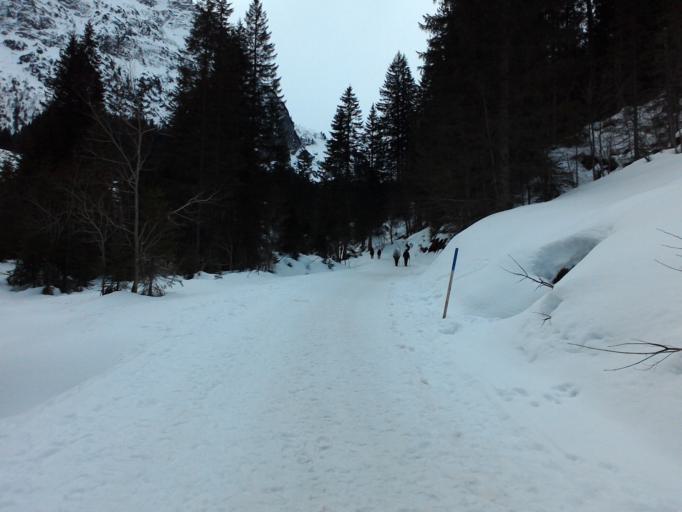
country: AT
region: Vorarlberg
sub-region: Politischer Bezirk Bregenz
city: Mittelberg
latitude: 47.3006
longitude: 10.1178
